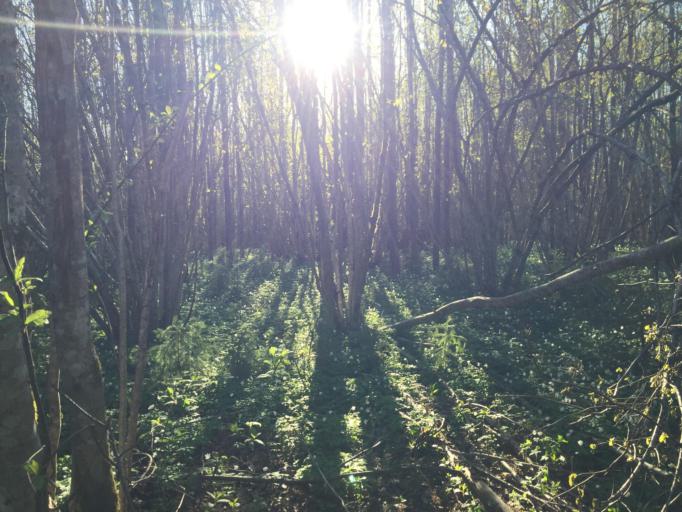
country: LV
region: Vecpiebalga
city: Vecpiebalga
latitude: 56.8675
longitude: 25.9476
